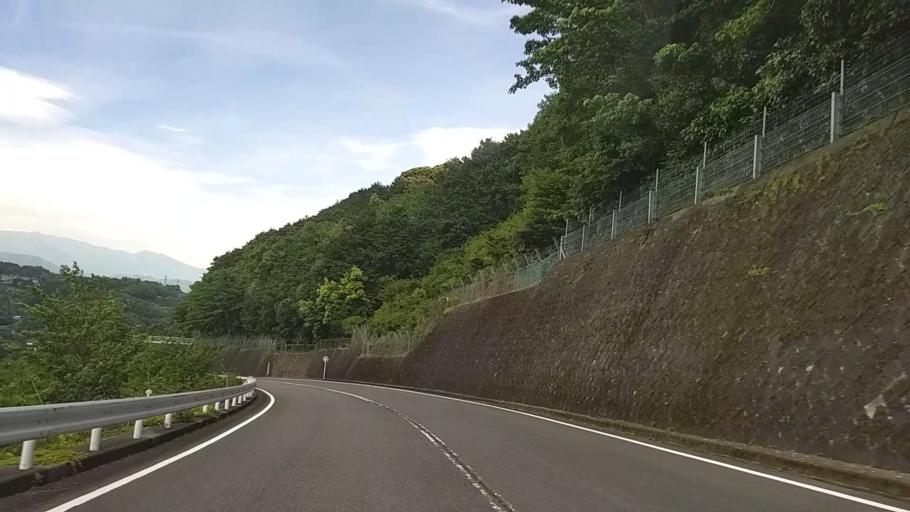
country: JP
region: Kanagawa
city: Odawara
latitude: 35.2405
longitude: 139.1291
